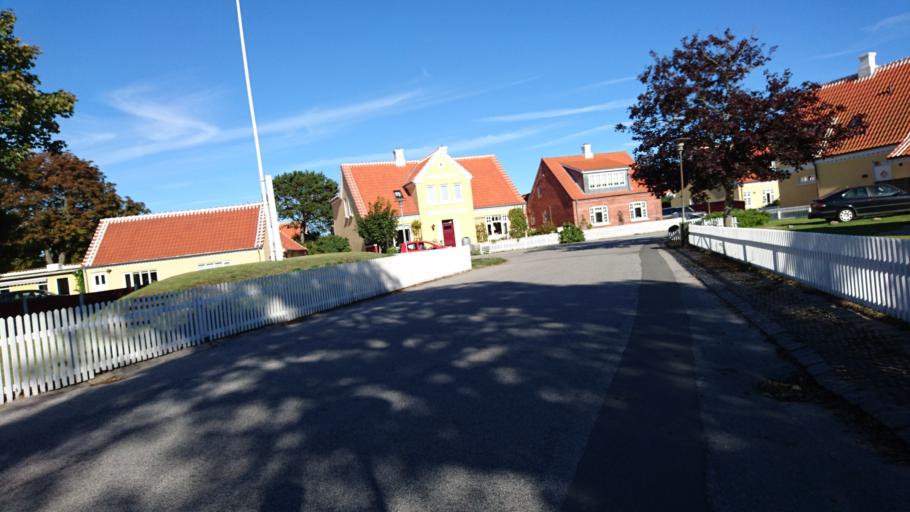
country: DK
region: North Denmark
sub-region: Frederikshavn Kommune
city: Skagen
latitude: 57.7246
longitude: 10.5987
